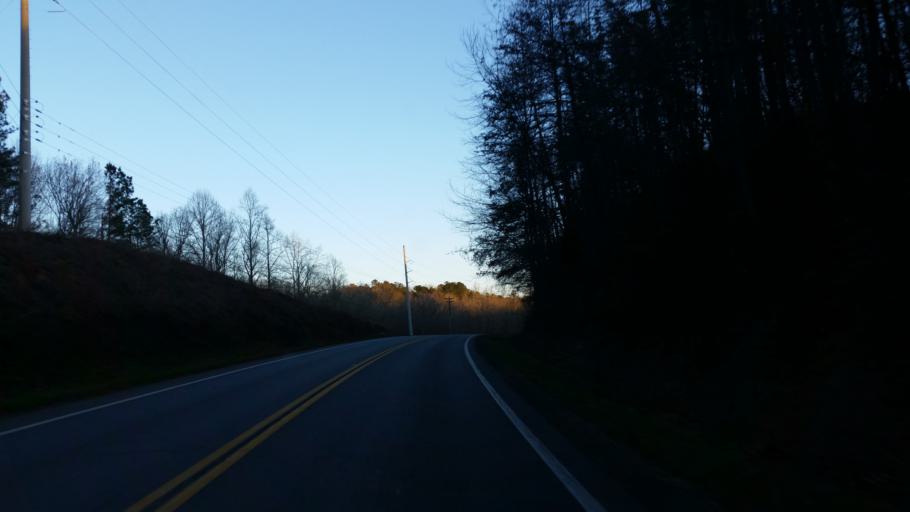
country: US
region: Georgia
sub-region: Dawson County
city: Dawsonville
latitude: 34.3305
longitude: -84.0115
